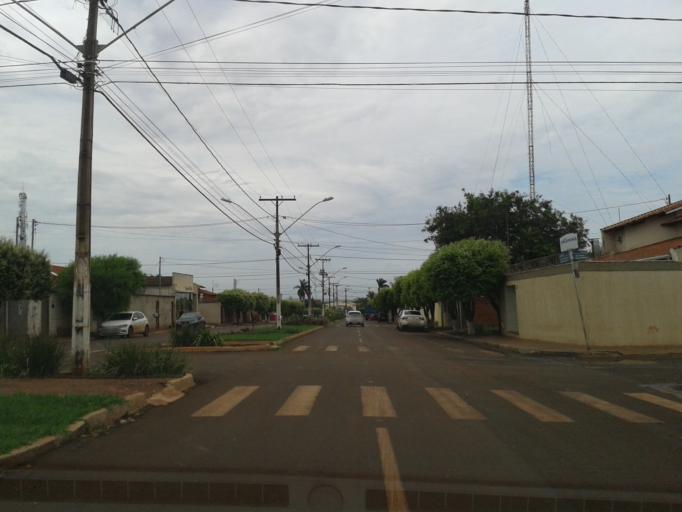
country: BR
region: Goias
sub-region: Itumbiara
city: Itumbiara
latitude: -18.4293
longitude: -49.1882
